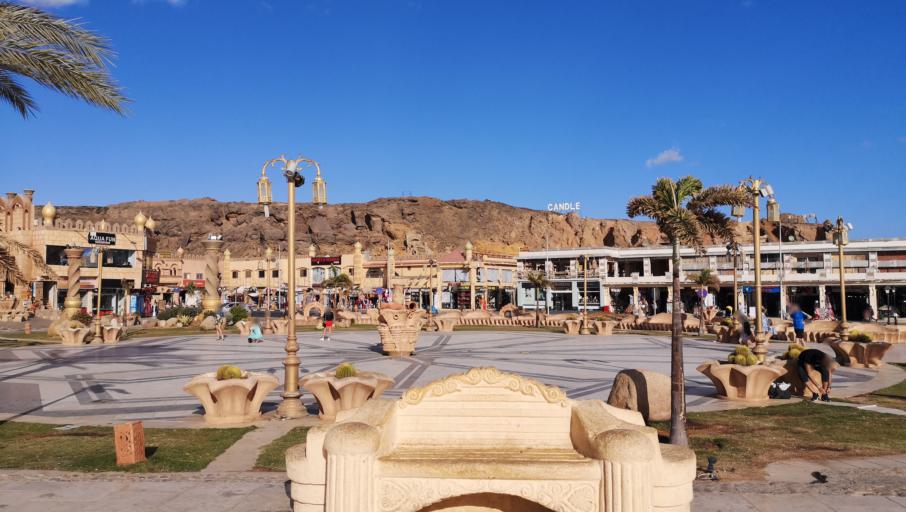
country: EG
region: South Sinai
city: Sharm el-Sheikh
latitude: 27.8657
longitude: 34.2951
